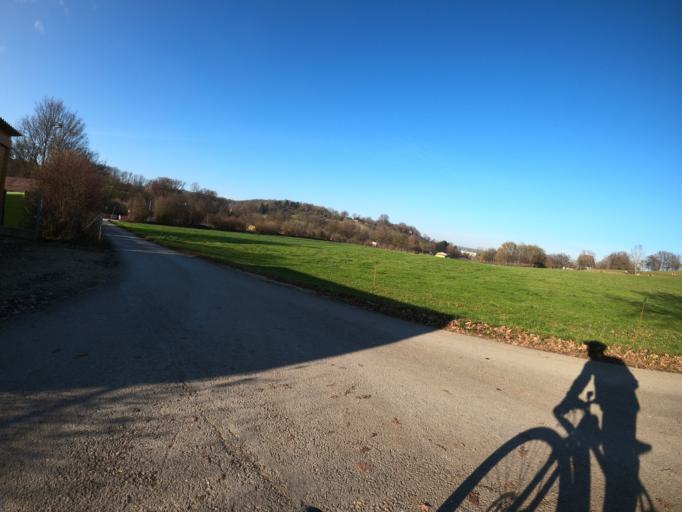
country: DE
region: Baden-Wuerttemberg
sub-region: Regierungsbezirk Stuttgart
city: Goeppingen
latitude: 48.6831
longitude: 9.6729
